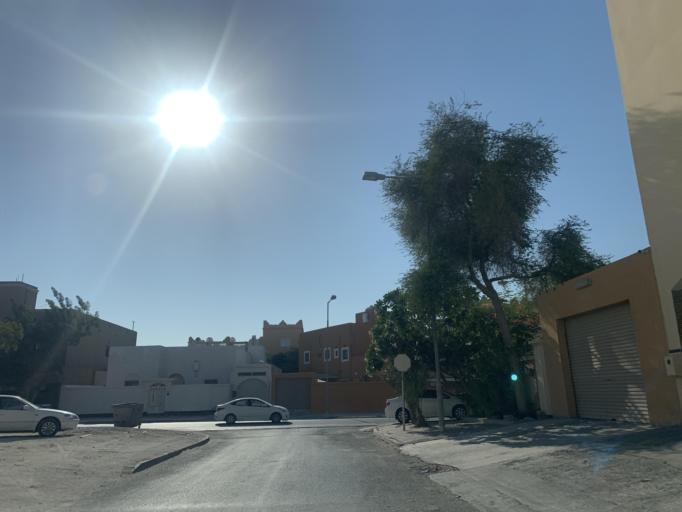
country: BH
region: Central Governorate
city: Madinat Hamad
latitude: 26.1047
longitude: 50.5094
